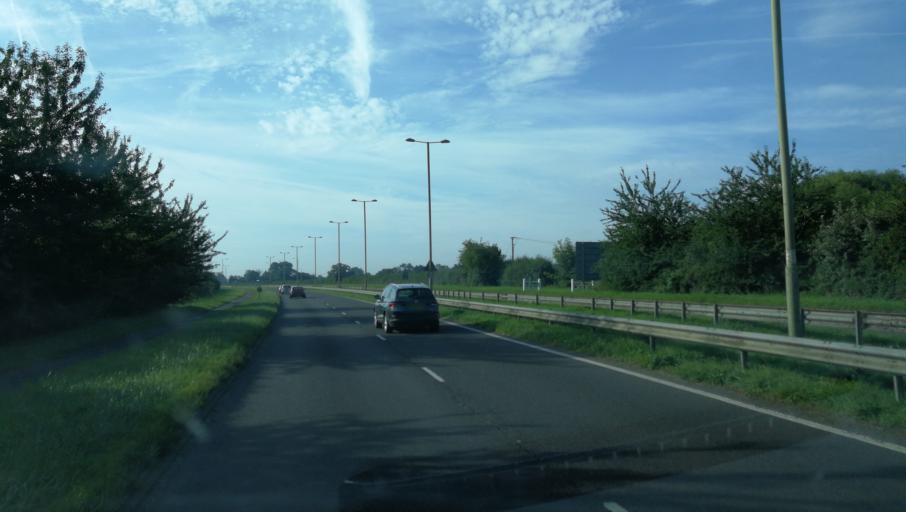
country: GB
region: England
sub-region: Oxfordshire
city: Yarnton
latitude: 51.8202
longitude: -1.3180
